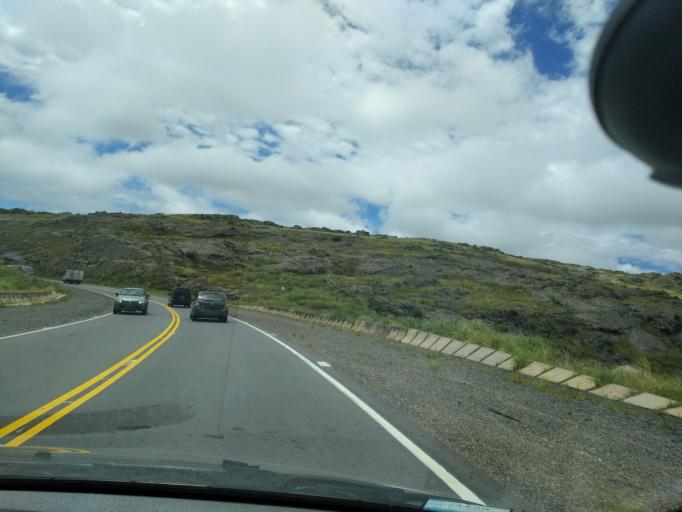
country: AR
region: Cordoba
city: Cuesta Blanca
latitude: -31.6012
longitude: -64.7135
